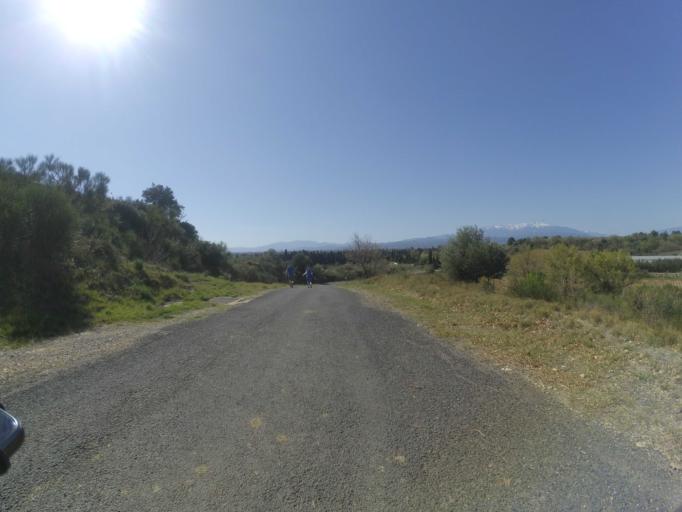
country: FR
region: Languedoc-Roussillon
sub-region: Departement des Pyrenees-Orientales
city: Pezilla-la-Riviere
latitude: 42.7073
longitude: 2.7752
